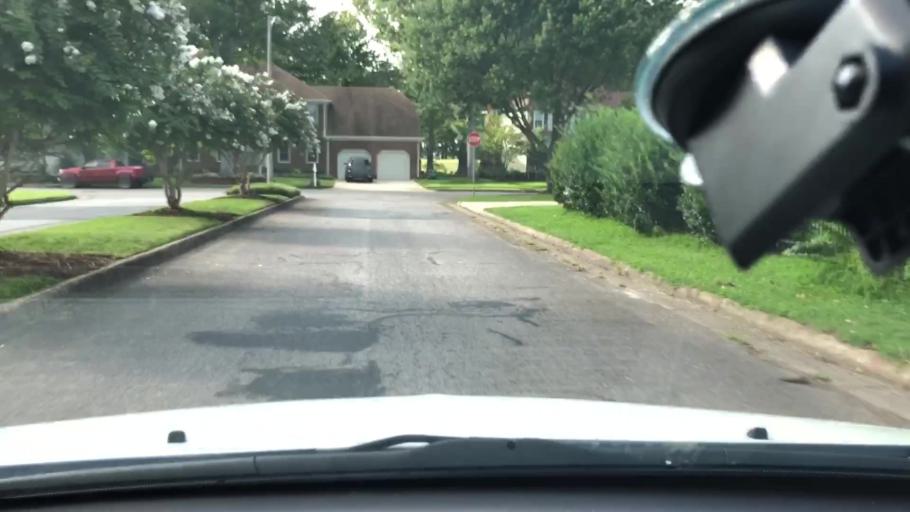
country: US
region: Virginia
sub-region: City of Chesapeake
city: Chesapeake
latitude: 36.7075
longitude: -76.2822
